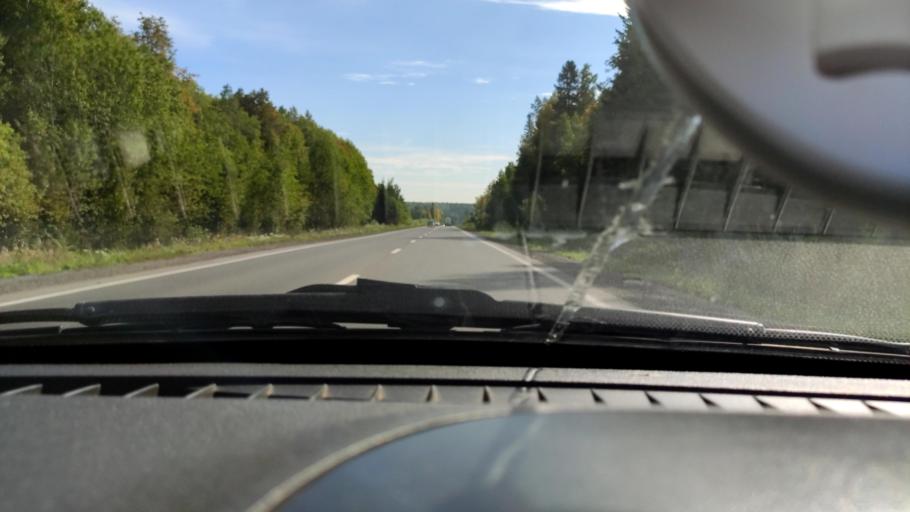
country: RU
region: Perm
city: Novyye Lyady
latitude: 58.0428
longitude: 56.4465
